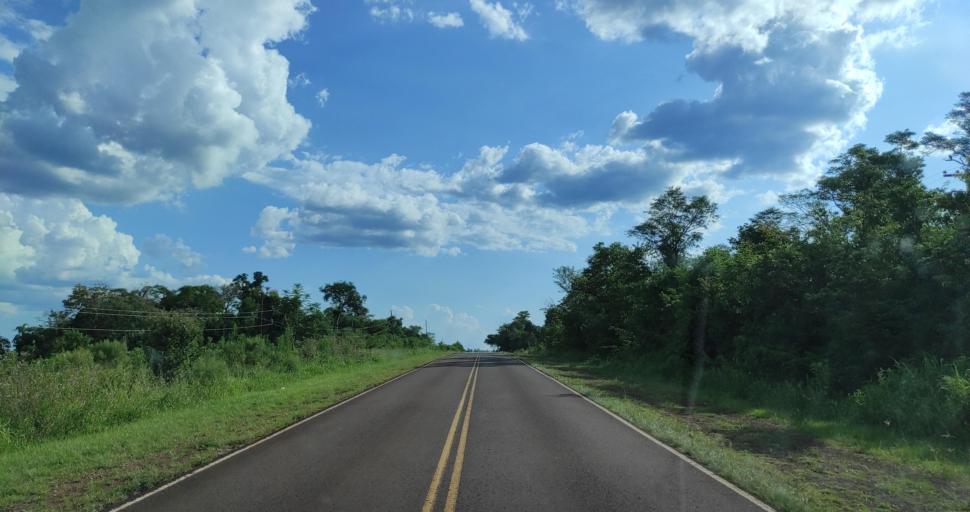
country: AR
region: Misiones
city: San Vicente
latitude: -26.3524
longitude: -54.2103
